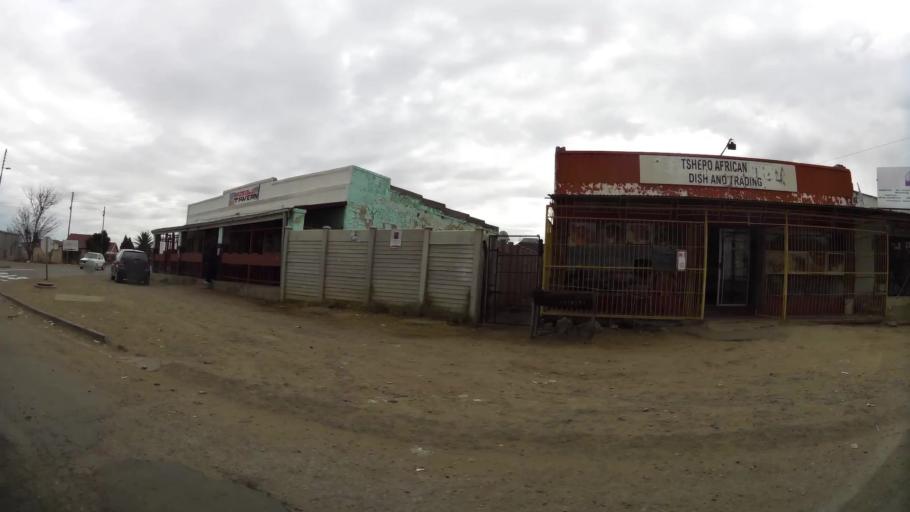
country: ZA
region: Orange Free State
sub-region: Fezile Dabi District Municipality
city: Kroonstad
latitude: -27.6512
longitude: 27.2081
